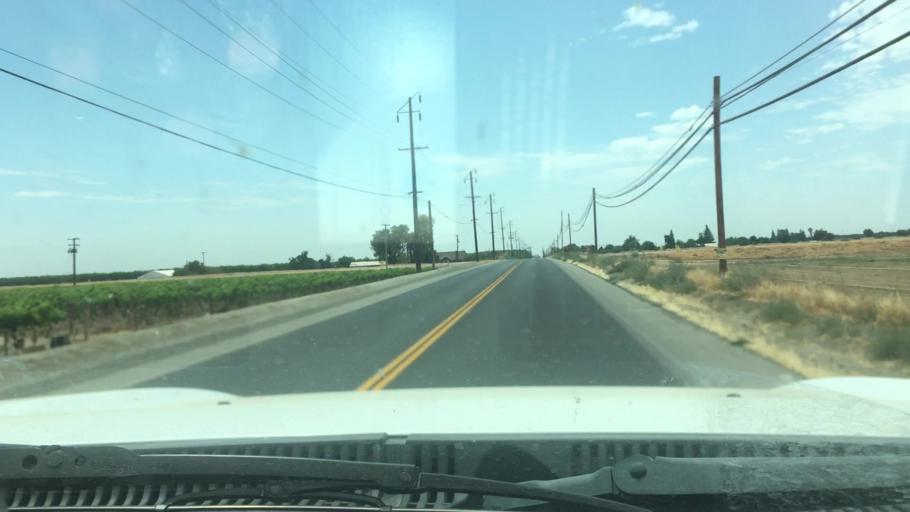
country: US
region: California
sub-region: Tulare County
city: Poplar-Cotton Center
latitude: 36.0659
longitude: -119.0907
